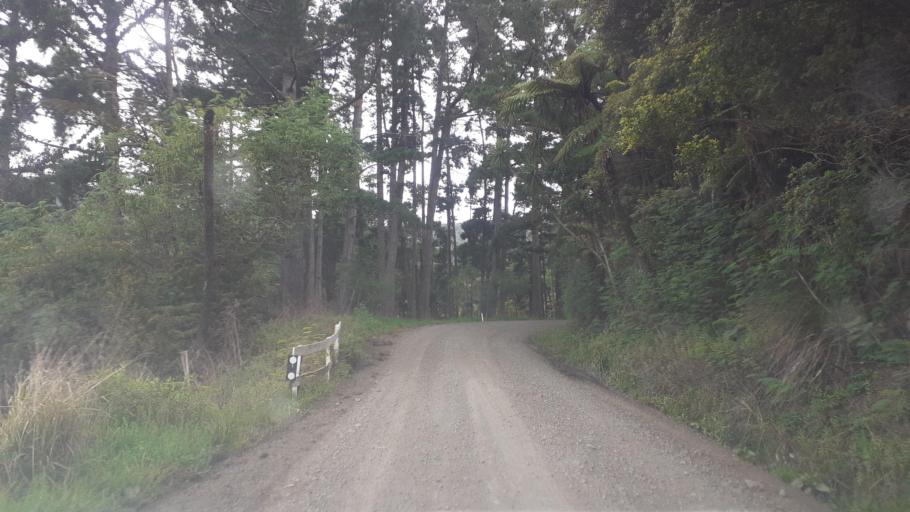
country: NZ
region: Northland
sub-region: Far North District
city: Waimate North
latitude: -35.5669
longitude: 173.5321
